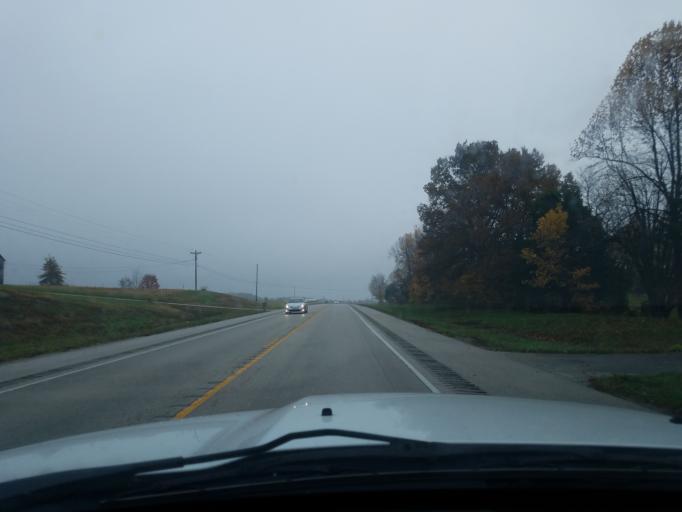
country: US
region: Kentucky
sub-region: Green County
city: Greensburg
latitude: 37.4169
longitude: -85.5060
